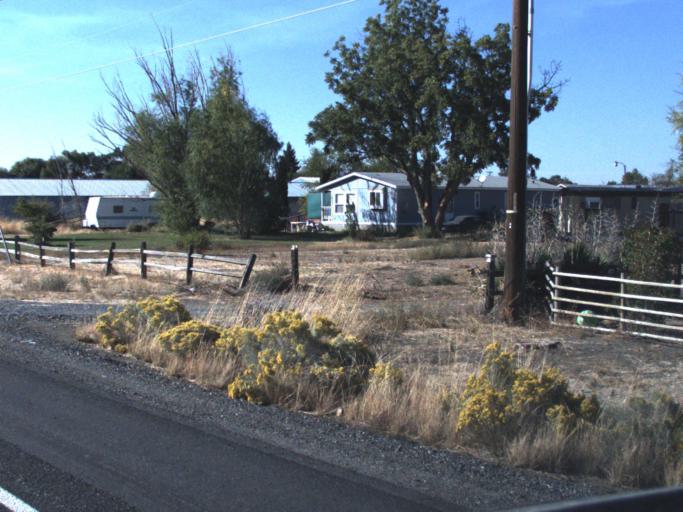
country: US
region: Washington
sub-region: Benton County
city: Finley
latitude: 46.1479
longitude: -119.0168
